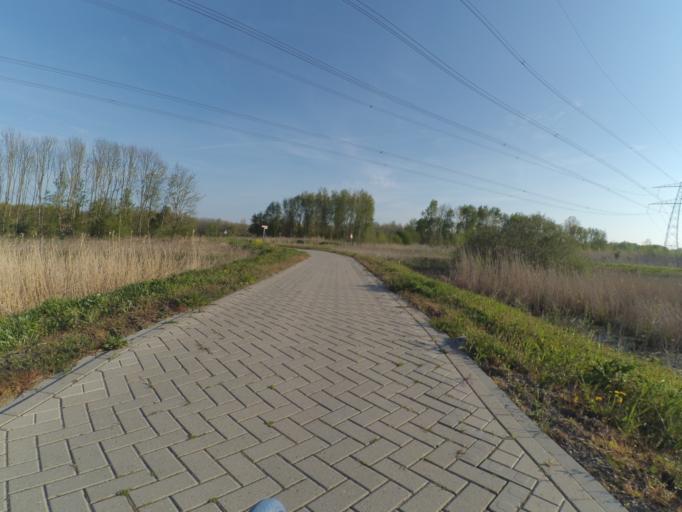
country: NL
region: Flevoland
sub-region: Gemeente Almere
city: Almere Stad
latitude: 52.4071
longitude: 5.3549
